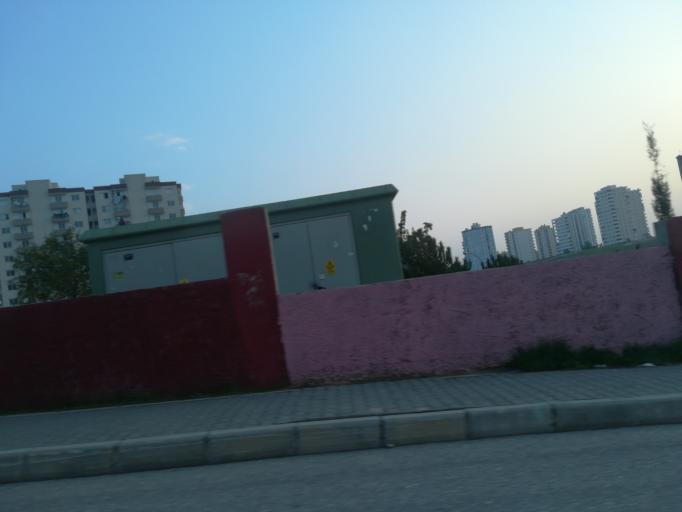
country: TR
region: Adana
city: Adana
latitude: 37.0786
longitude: 35.4130
